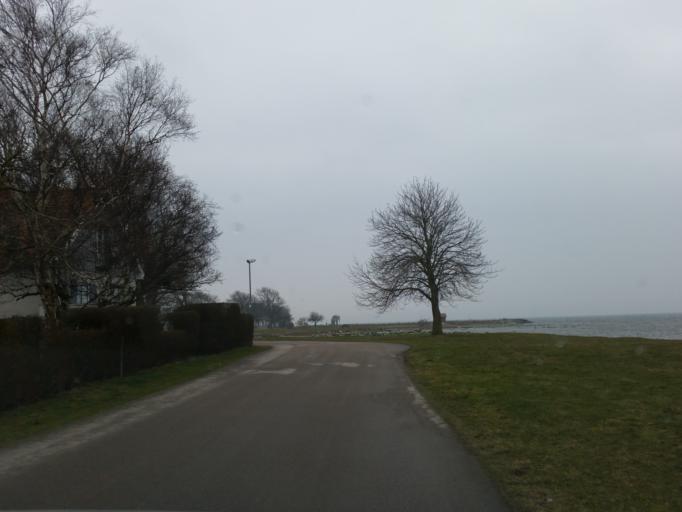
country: SE
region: Kalmar
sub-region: Morbylanga Kommun
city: Moerbylanga
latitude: 56.5256
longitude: 16.3719
